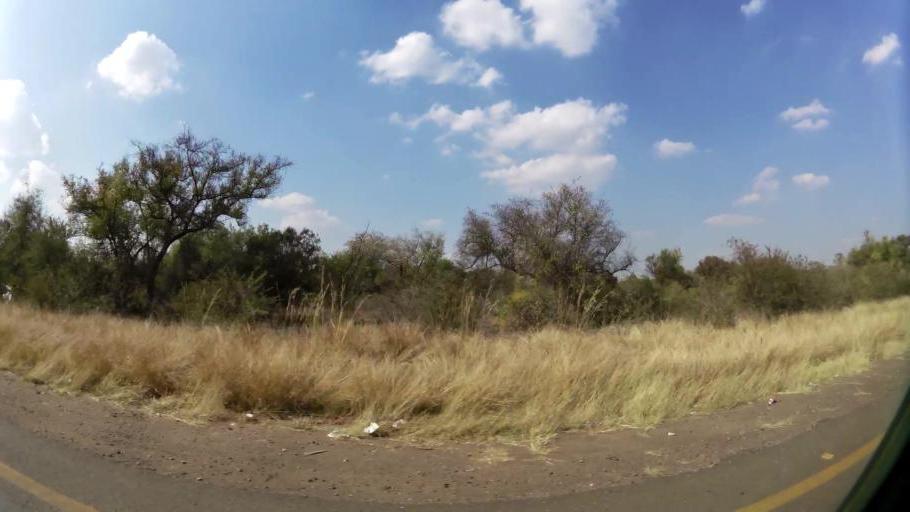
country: ZA
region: North-West
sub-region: Bojanala Platinum District Municipality
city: Mogwase
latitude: -25.4536
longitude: 27.0878
